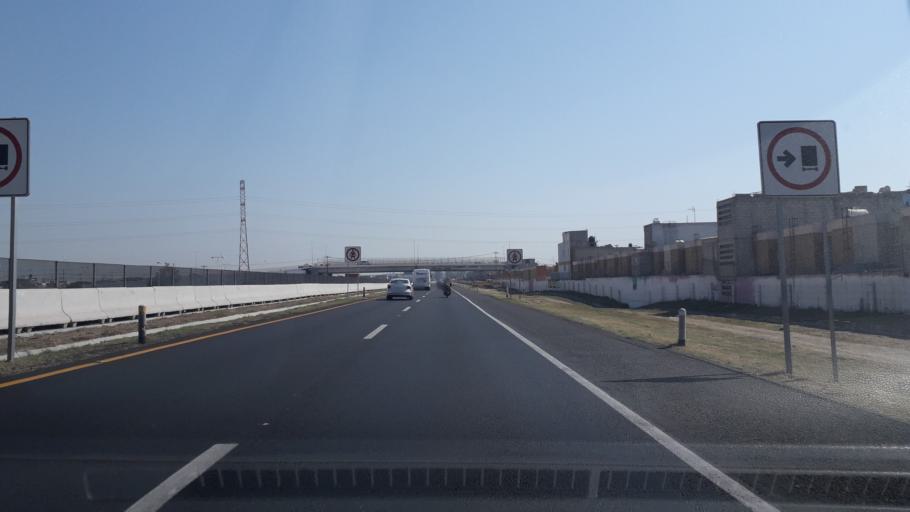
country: MX
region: Mexico
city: Santo Tomas Chiconautla
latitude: 19.6297
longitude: -99.0236
